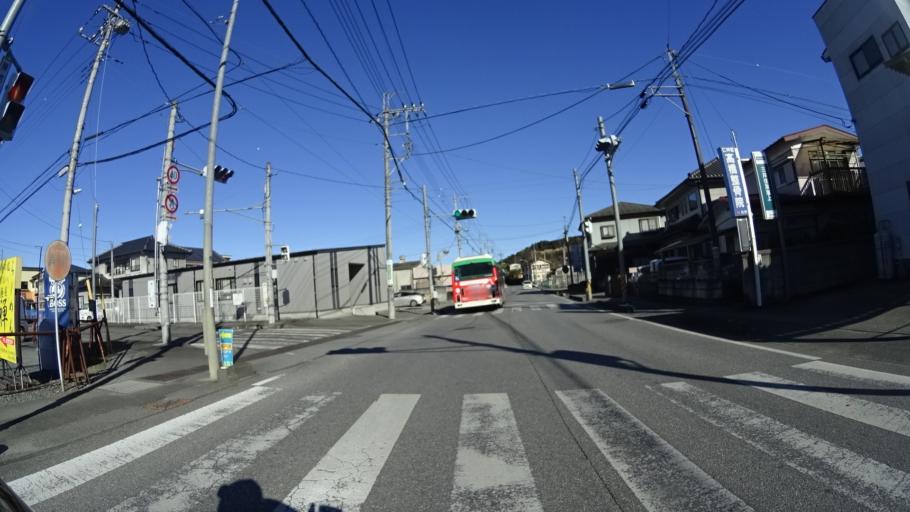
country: JP
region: Tochigi
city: Kanuma
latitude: 36.5793
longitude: 139.7656
